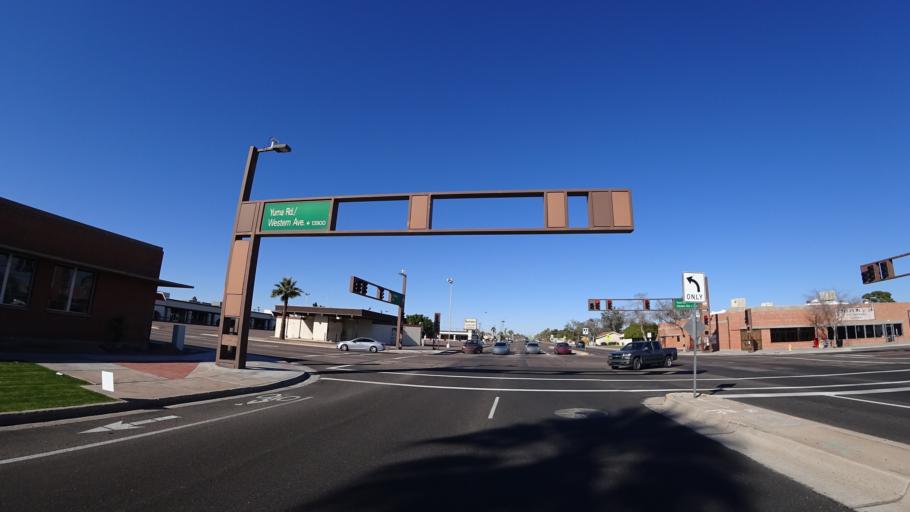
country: US
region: Arizona
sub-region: Maricopa County
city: Goodyear
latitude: 33.4351
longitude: -112.3584
